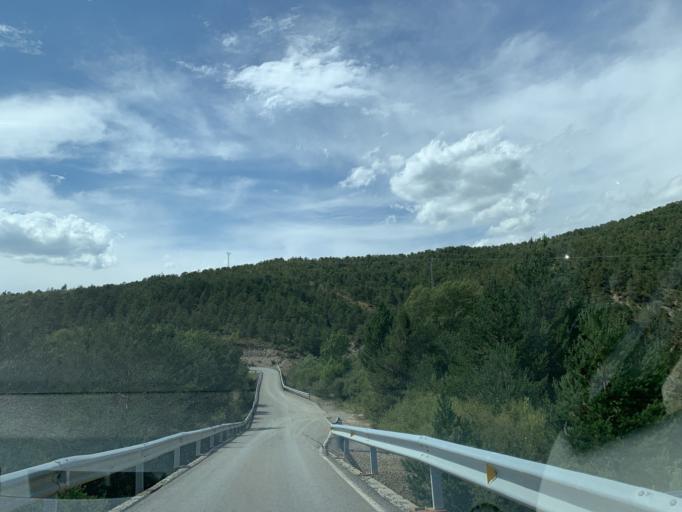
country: ES
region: Aragon
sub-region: Provincia de Huesca
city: Borau
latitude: 42.6560
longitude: -0.6325
